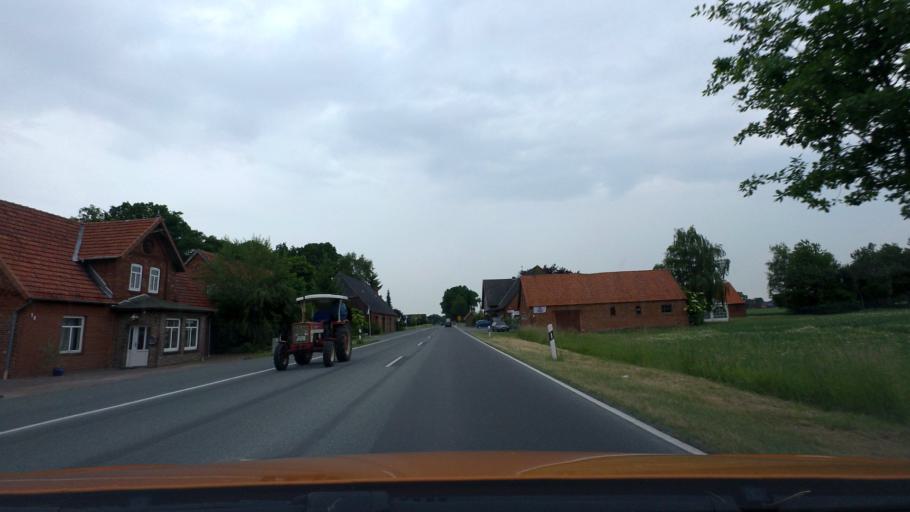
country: DE
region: Lower Saxony
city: Asendorf
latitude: 52.7519
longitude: 9.0195
